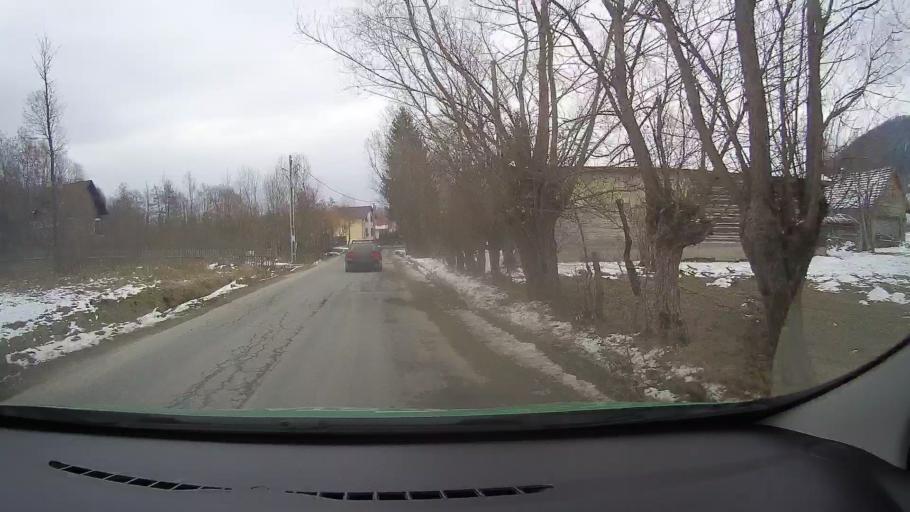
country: RO
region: Brasov
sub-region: Comuna Bran
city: Bran
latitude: 45.5299
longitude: 25.3549
